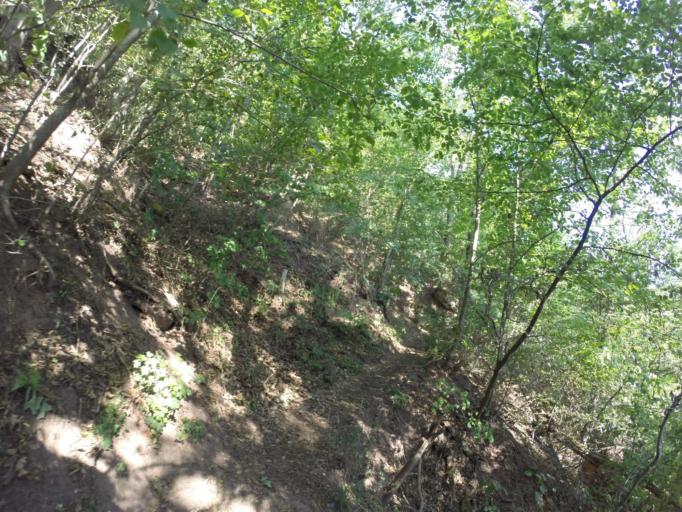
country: DE
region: Thuringia
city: Sulza
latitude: 50.8544
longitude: 11.6209
